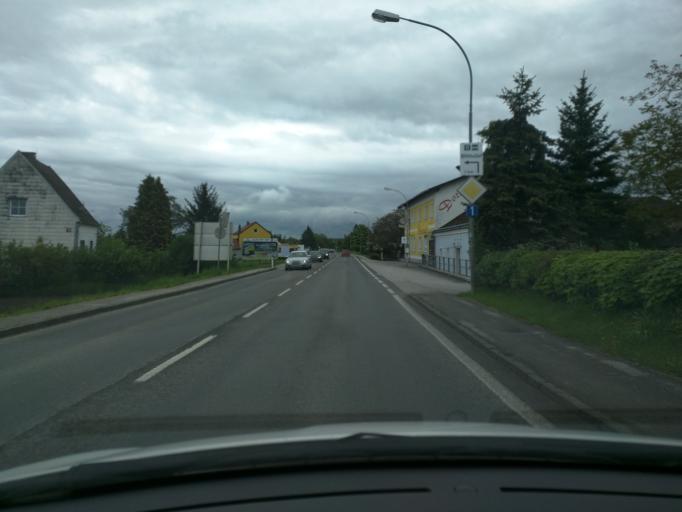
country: AT
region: Lower Austria
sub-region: Politischer Bezirk Amstetten
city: Euratsfeld
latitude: 48.1157
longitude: 14.9122
